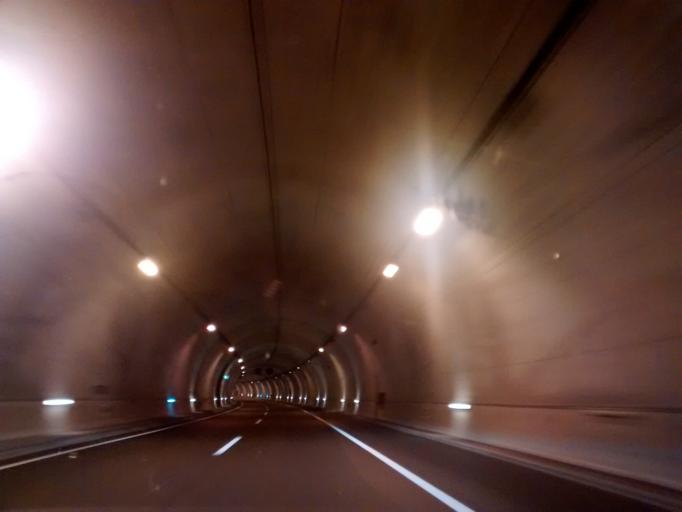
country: ES
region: Cantabria
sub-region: Provincia de Cantabria
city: Pesquera
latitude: 43.0890
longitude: -4.0793
